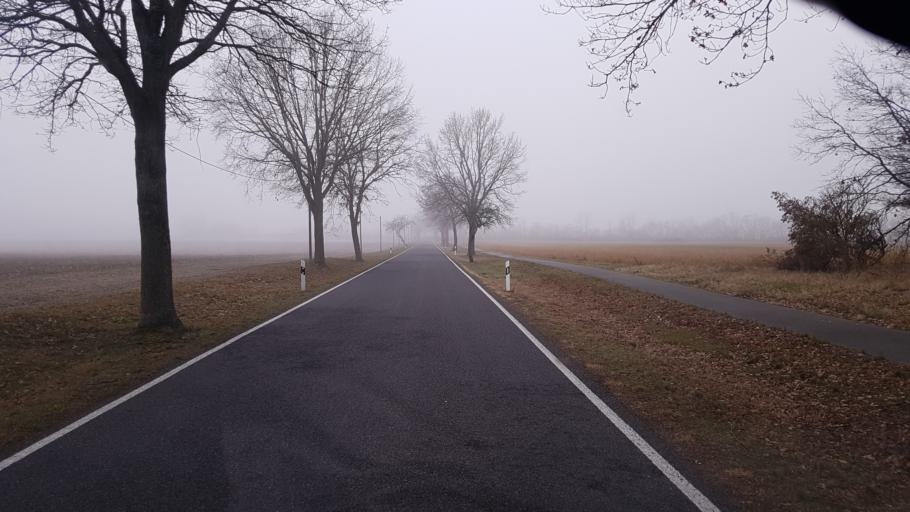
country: DE
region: Saxony-Anhalt
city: Holzdorf
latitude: 51.8544
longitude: 13.2119
